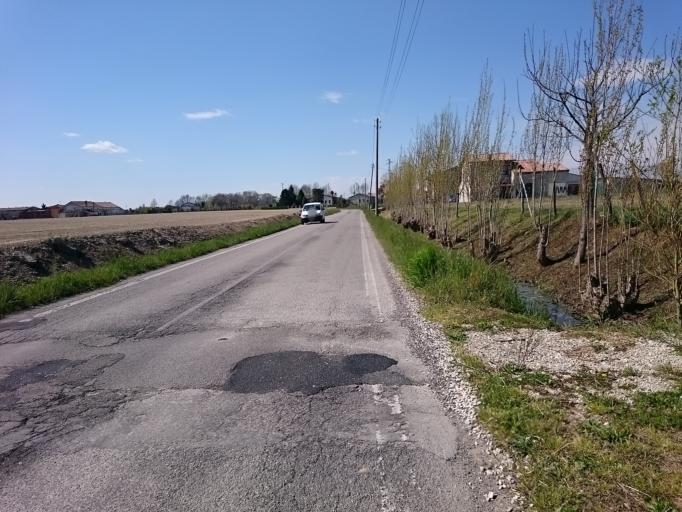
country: IT
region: Veneto
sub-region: Provincia di Padova
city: Campagnola
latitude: 45.2907
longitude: 12.0093
